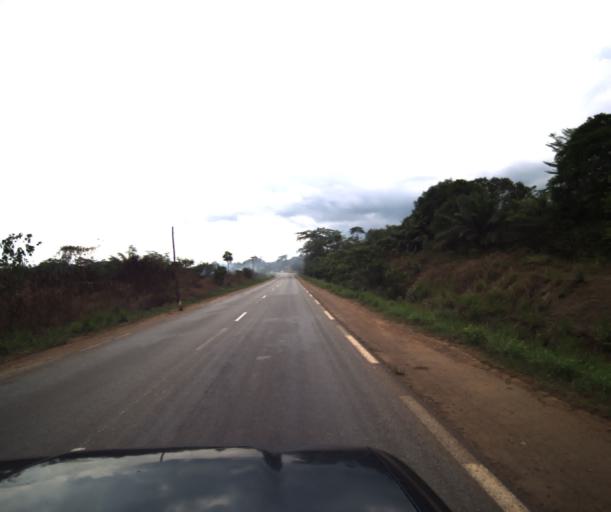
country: CM
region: Littoral
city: Edea
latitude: 3.9494
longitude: 10.0339
